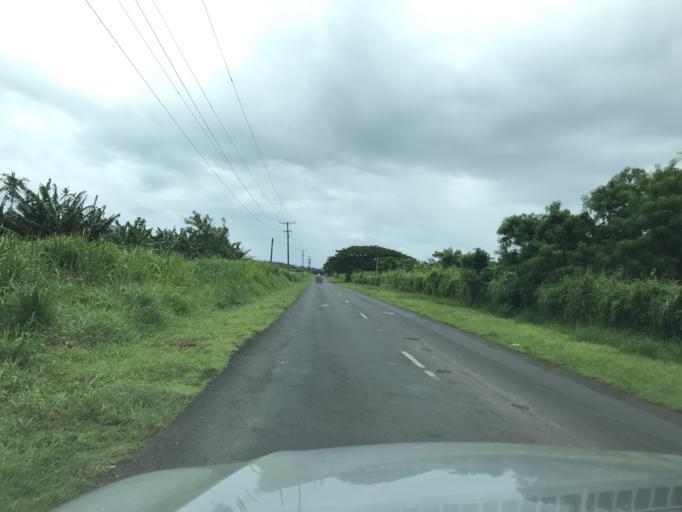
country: WS
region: Aiga-i-le-Tai
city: Mulifanua
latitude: -13.8332
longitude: -172.0220
